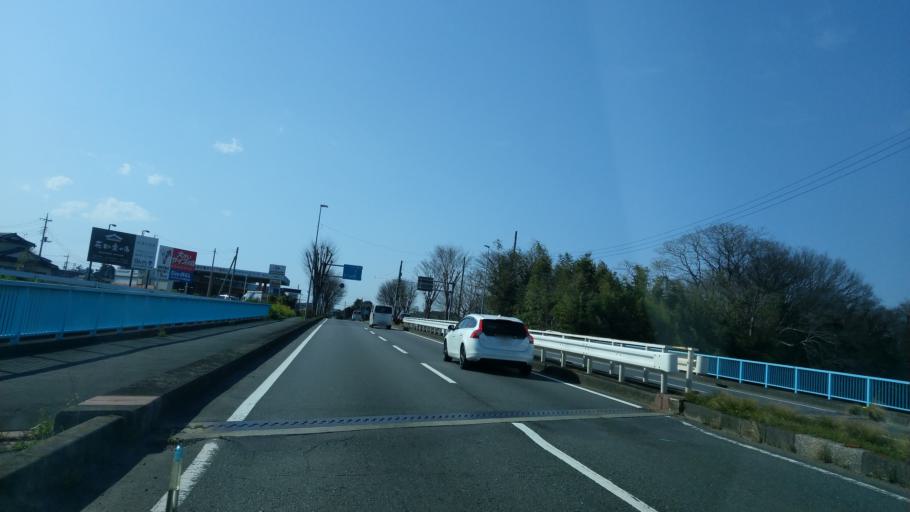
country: JP
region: Saitama
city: Sakado
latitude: 36.0091
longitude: 139.4402
